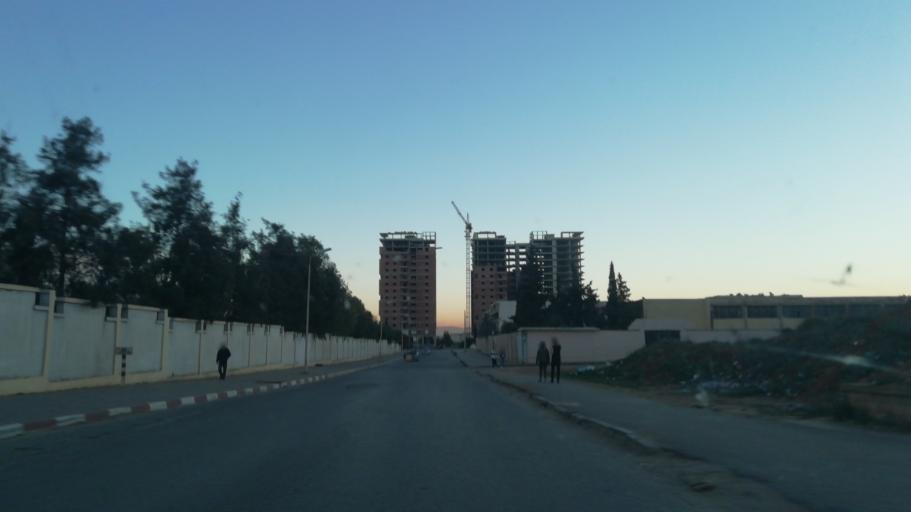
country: DZ
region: Oran
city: Bir el Djir
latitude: 35.7002
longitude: -0.5909
